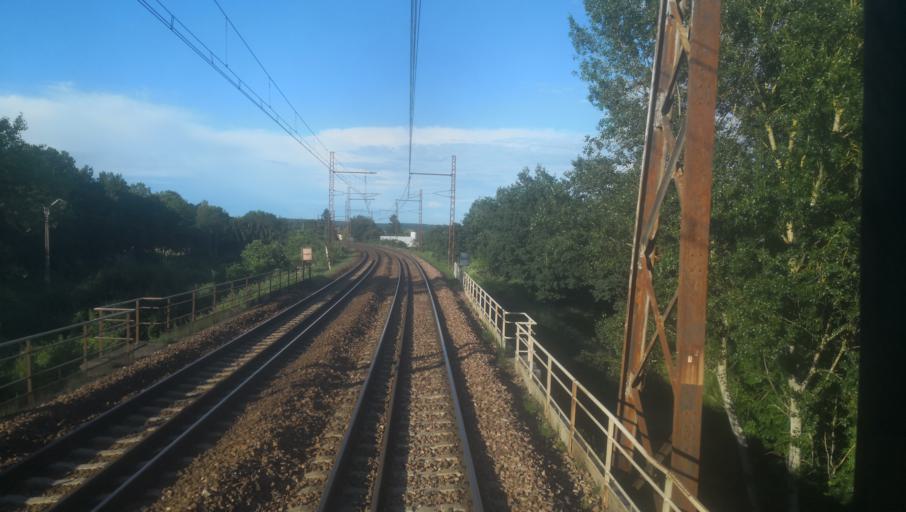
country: FR
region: Centre
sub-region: Departement du Cher
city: Vierzon
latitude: 47.1978
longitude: 2.0940
